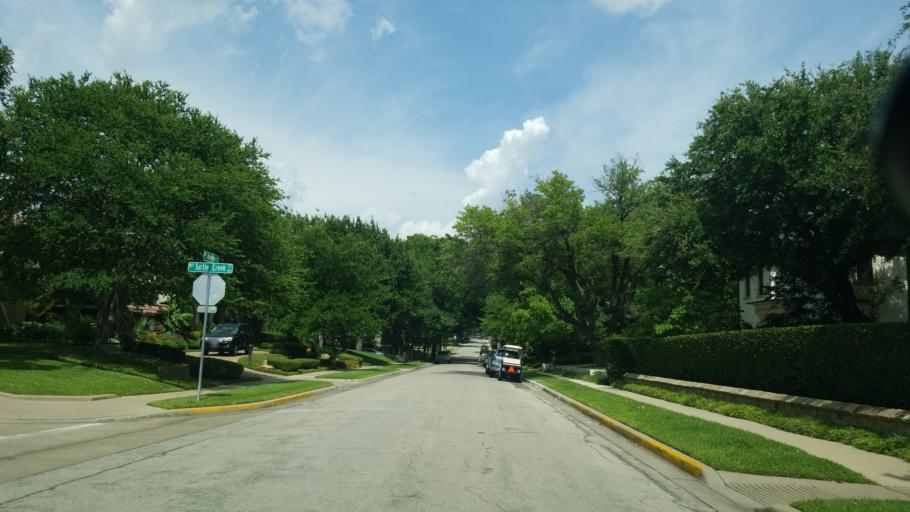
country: US
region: Texas
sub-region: Dallas County
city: University Park
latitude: 32.8521
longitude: -96.7948
